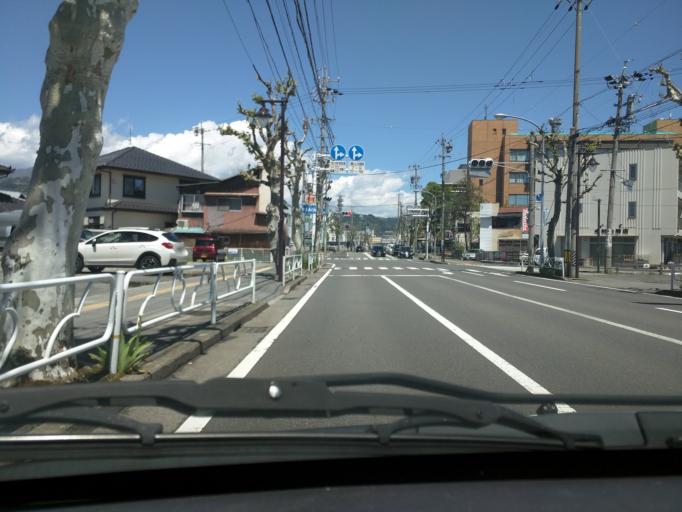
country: JP
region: Nagano
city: Nagano-shi
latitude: 36.6430
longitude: 138.1987
